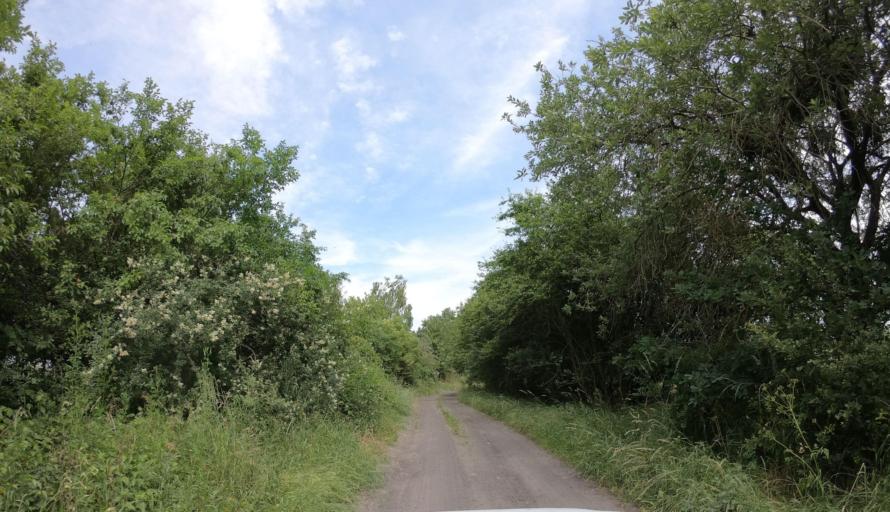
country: PL
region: West Pomeranian Voivodeship
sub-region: Powiat pyrzycki
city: Kozielice
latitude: 53.0346
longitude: 14.7614
